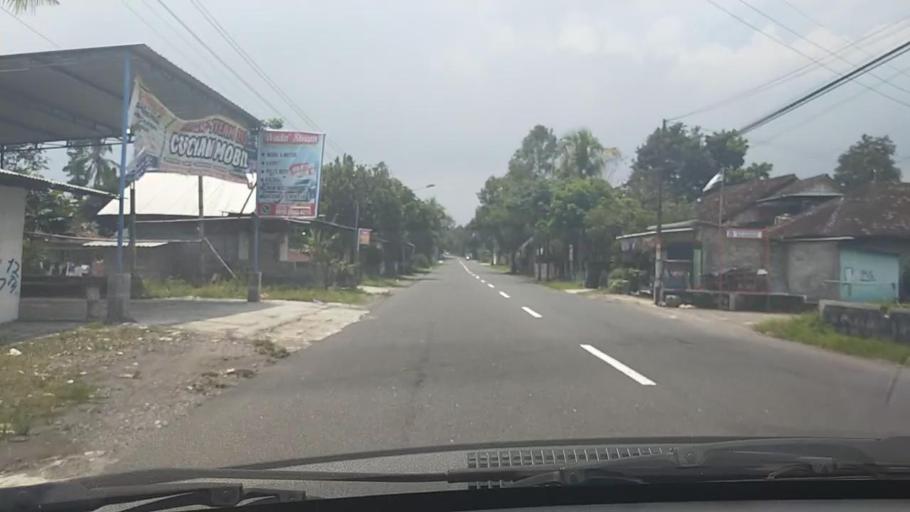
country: ID
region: Daerah Istimewa Yogyakarta
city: Sleman
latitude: -7.6941
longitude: 110.3884
